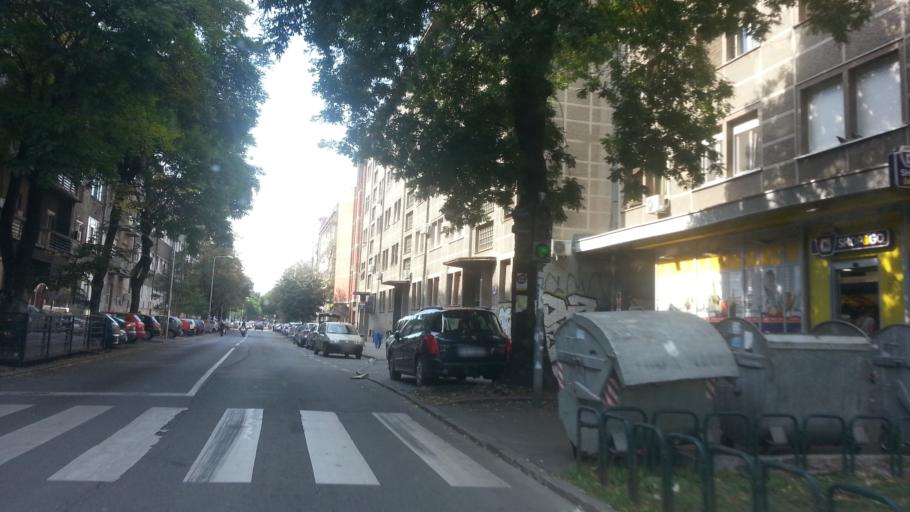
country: RS
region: Central Serbia
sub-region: Belgrade
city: Zemun
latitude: 44.8378
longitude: 20.4161
